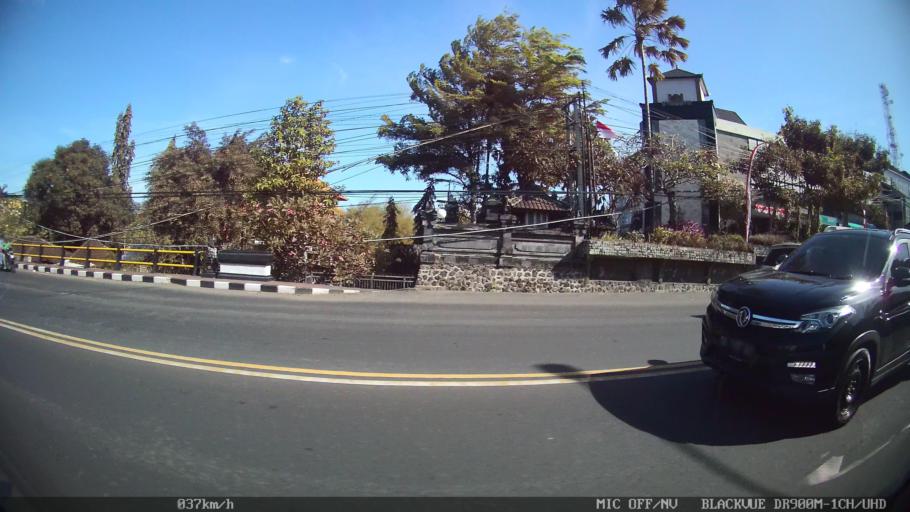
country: ID
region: Bali
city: Banjar Kertasari
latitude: -8.6364
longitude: 115.1930
